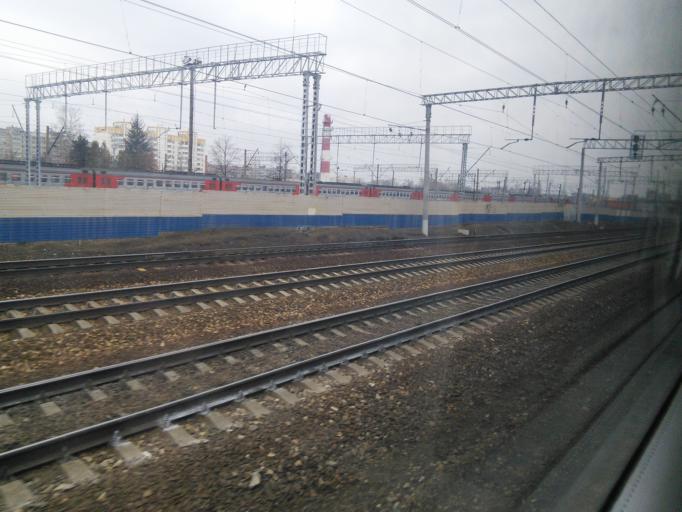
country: RU
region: Moskovskaya
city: Domodedovo
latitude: 55.4286
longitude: 37.7813
